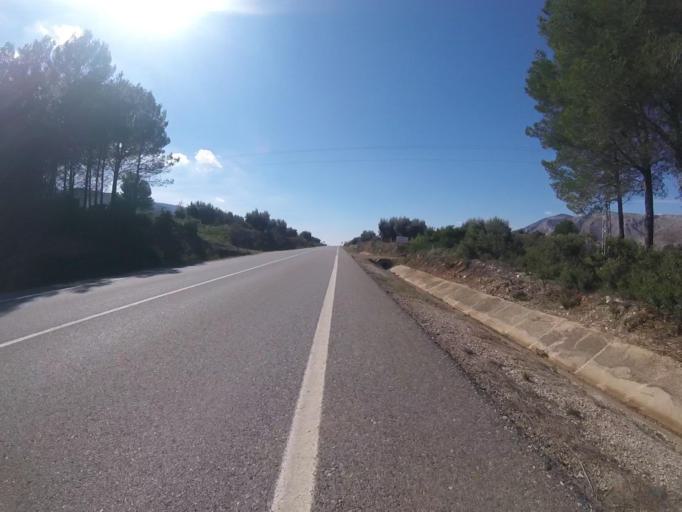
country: ES
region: Valencia
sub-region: Provincia de Castello
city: Sierra-Engarceran
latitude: 40.3189
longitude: -0.0283
